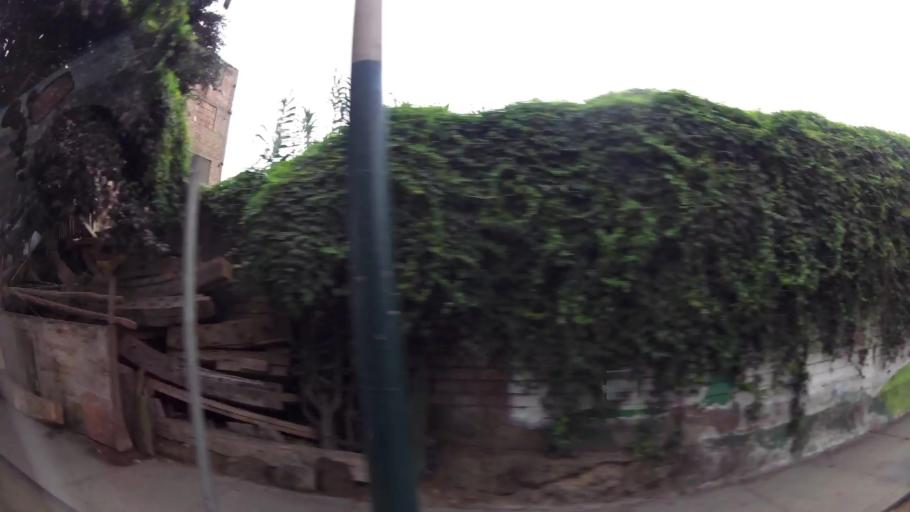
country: PE
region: Lima
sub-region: Lima
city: Surco
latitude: -12.1465
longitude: -77.0015
